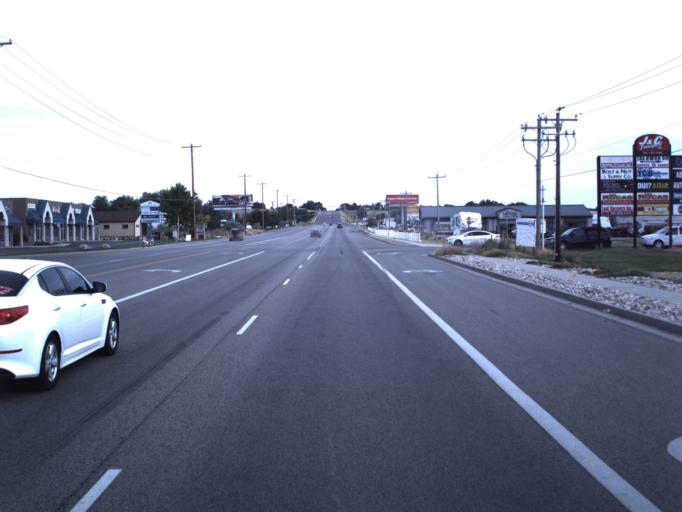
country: US
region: Utah
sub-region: Weber County
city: West Haven
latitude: 41.2105
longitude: -112.0259
